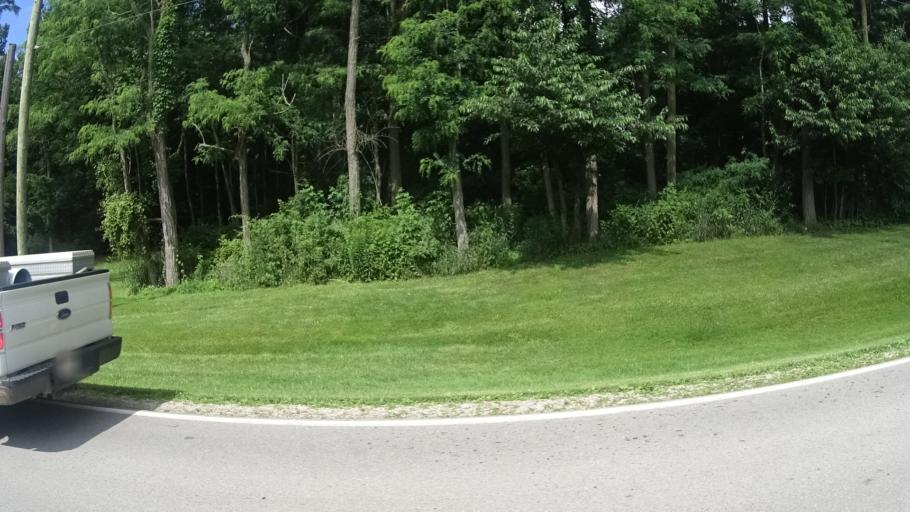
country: US
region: Ohio
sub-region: Huron County
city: Wakeman
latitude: 41.3119
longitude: -82.4135
